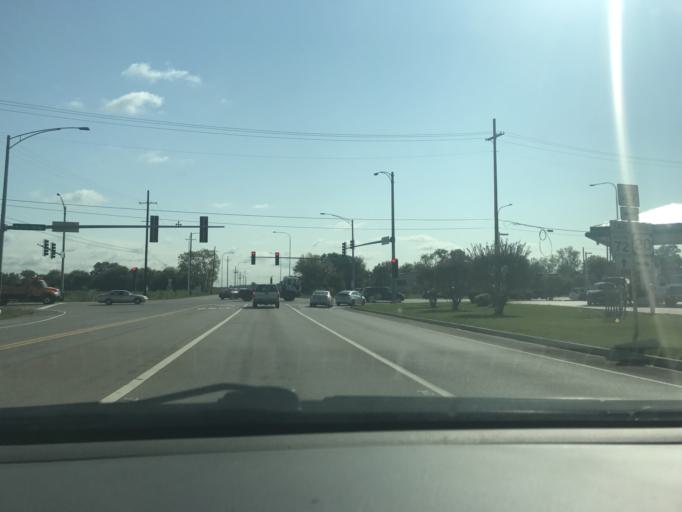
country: US
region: Illinois
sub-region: Kane County
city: Pingree Grove
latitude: 42.0885
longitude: -88.4577
